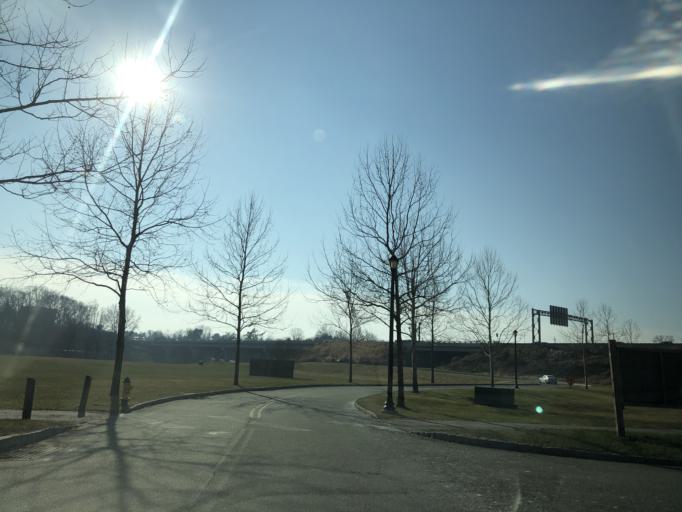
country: US
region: Pennsylvania
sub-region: Montgomery County
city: Audubon
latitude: 40.1104
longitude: -75.4181
